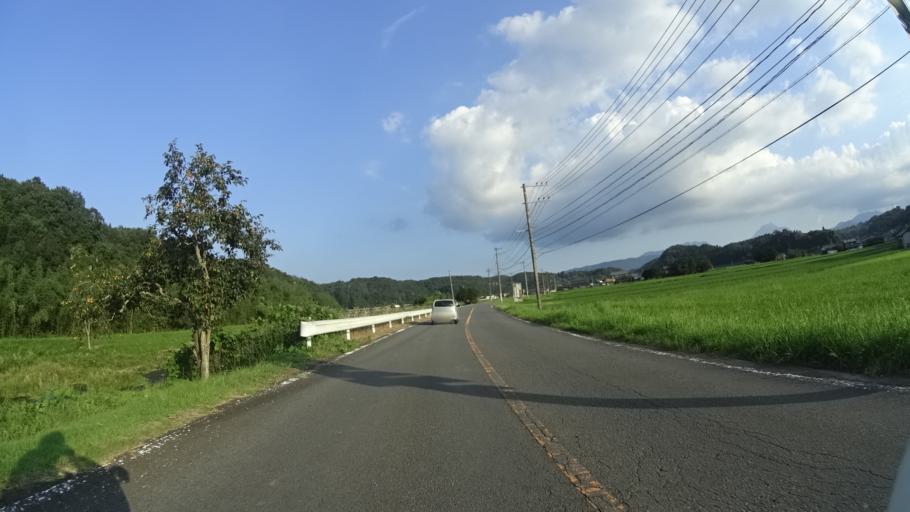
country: JP
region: Oita
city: Bungo-Takada-shi
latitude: 33.4232
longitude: 131.3772
